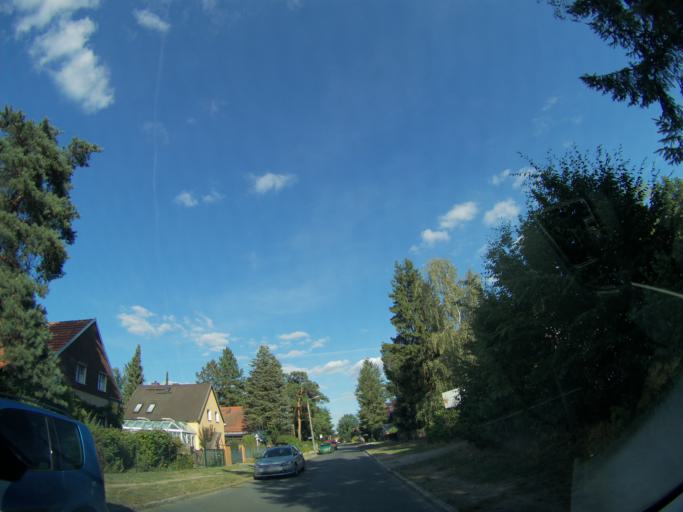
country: DE
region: Brandenburg
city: Stahnsdorf
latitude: 52.3816
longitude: 13.1978
